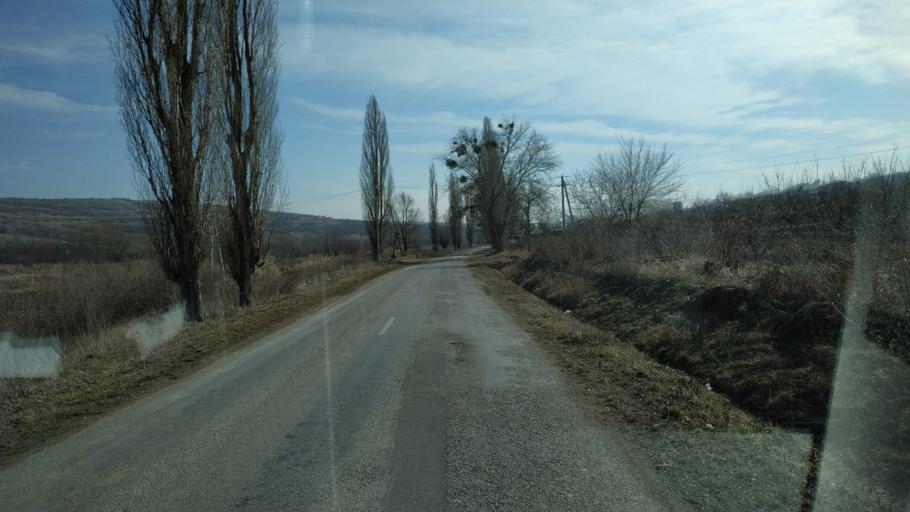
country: MD
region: Nisporeni
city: Nisporeni
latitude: 47.1623
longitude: 28.1026
